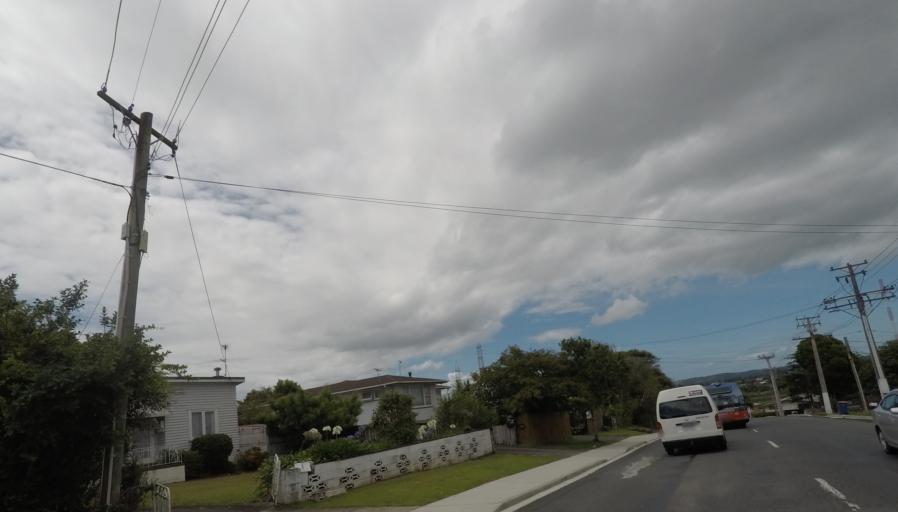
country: NZ
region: Auckland
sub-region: Auckland
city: Rosebank
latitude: -36.8462
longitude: 174.6235
